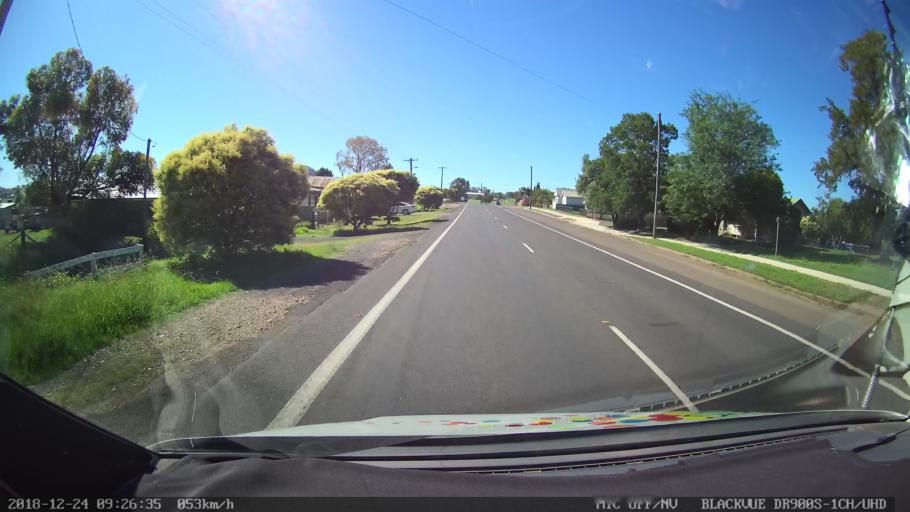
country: AU
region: New South Wales
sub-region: Liverpool Plains
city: Quirindi
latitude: -31.5209
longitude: 150.6774
